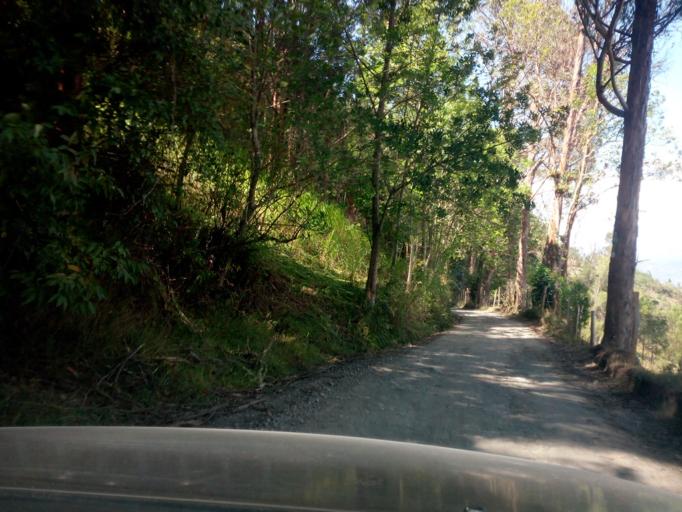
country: CO
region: Boyaca
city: Somondoco
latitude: 4.9733
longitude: -73.4066
